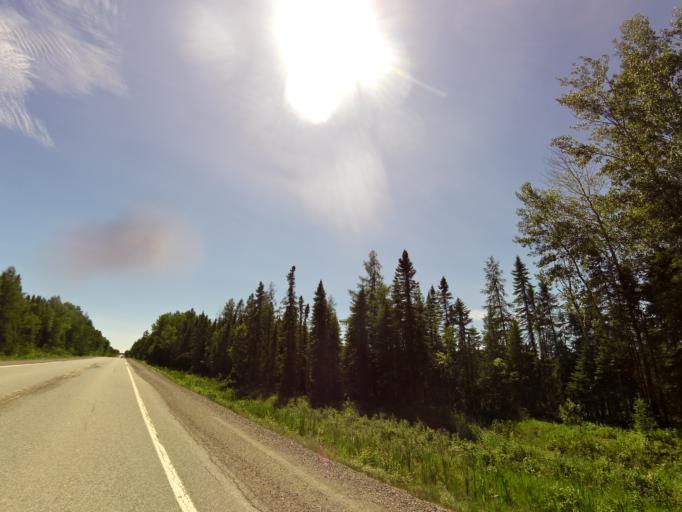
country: CA
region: Quebec
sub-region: Nord-du-Quebec
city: Lebel-sur-Quevillon
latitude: 48.8356
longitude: -77.1114
